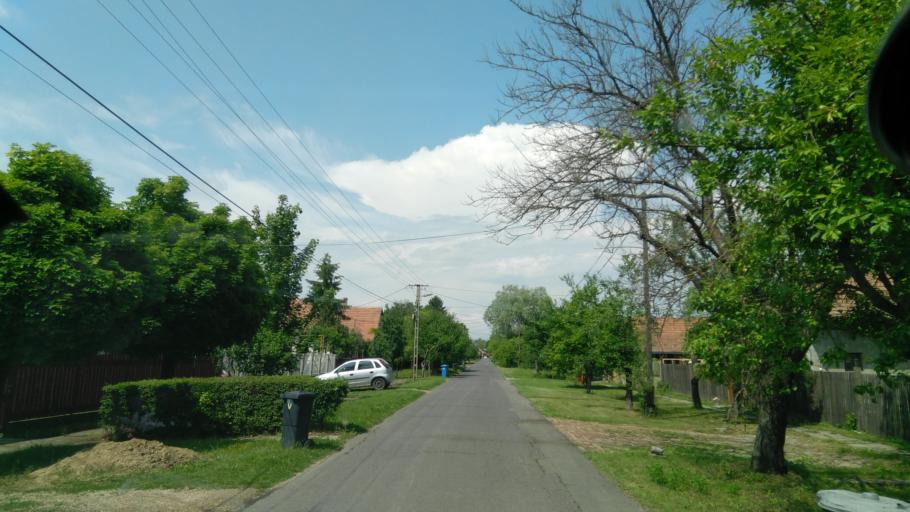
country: HU
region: Bekes
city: Bekes
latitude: 46.7600
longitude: 21.1471
